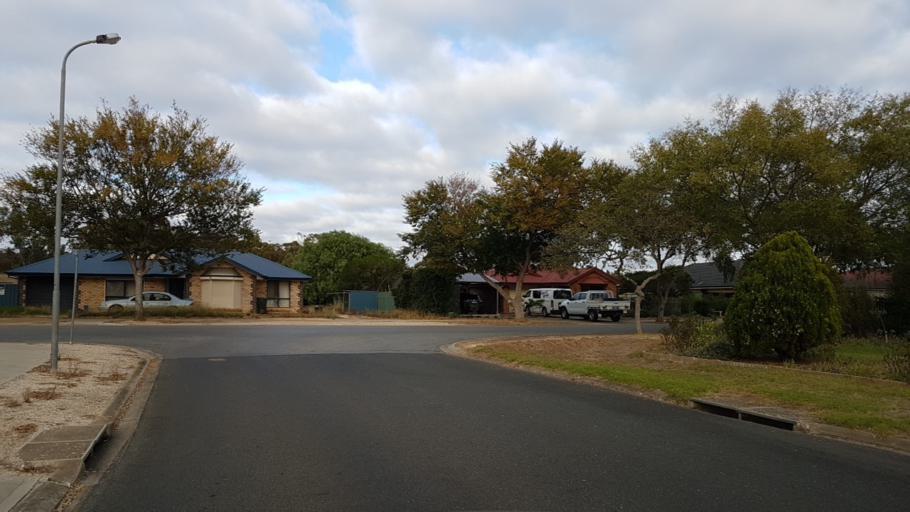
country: AU
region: South Australia
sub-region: Alexandrina
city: Strathalbyn
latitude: -35.2644
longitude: 138.9023
